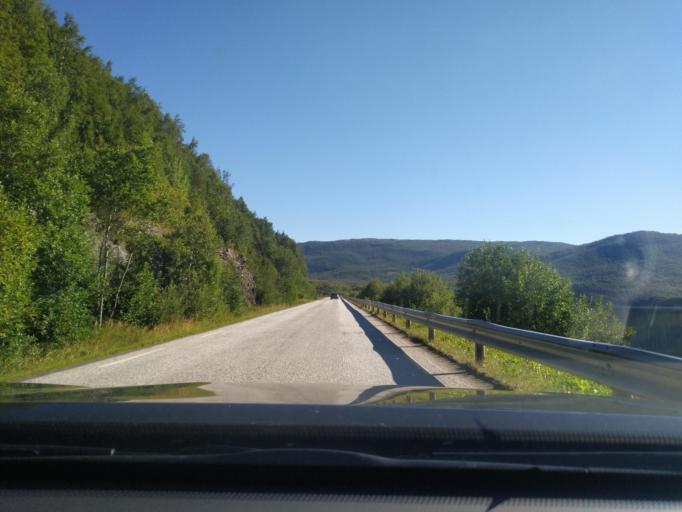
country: NO
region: Troms
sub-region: Dyroy
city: Brostadbotn
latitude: 68.9321
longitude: 17.6798
